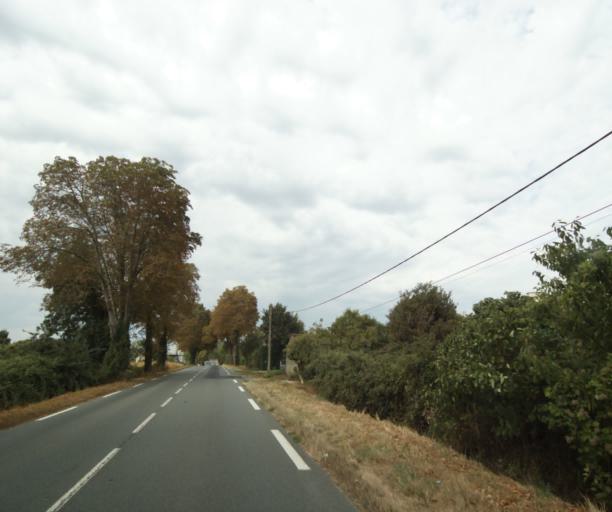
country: FR
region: Poitou-Charentes
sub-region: Departement de la Charente-Maritime
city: Tonnay-Charente
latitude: 45.9549
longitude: -0.8696
